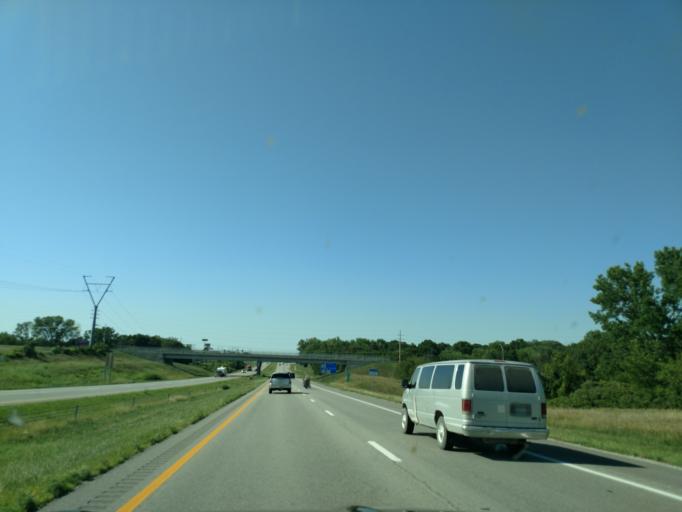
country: US
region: Missouri
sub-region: Buchanan County
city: Saint Joseph
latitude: 39.7679
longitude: -94.7922
